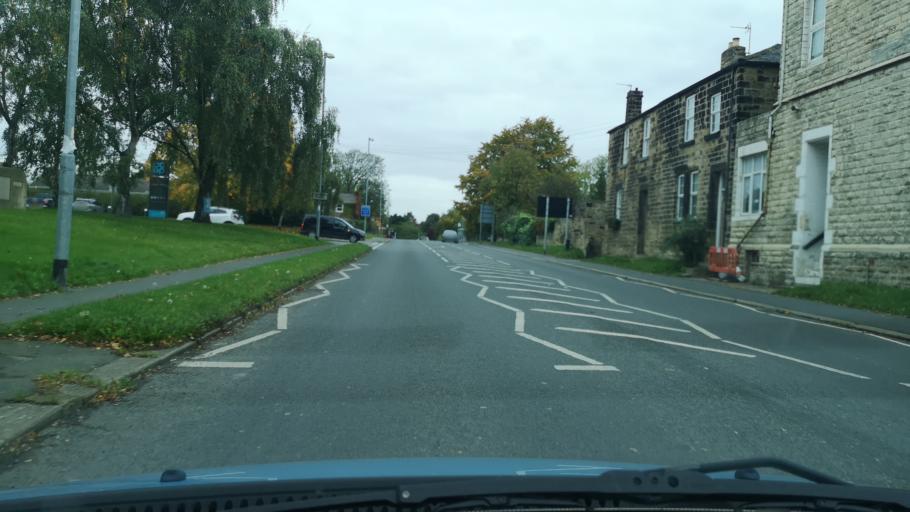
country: GB
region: England
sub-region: City and Borough of Wakefield
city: Low Ackworth
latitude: 53.6417
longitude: -1.3368
